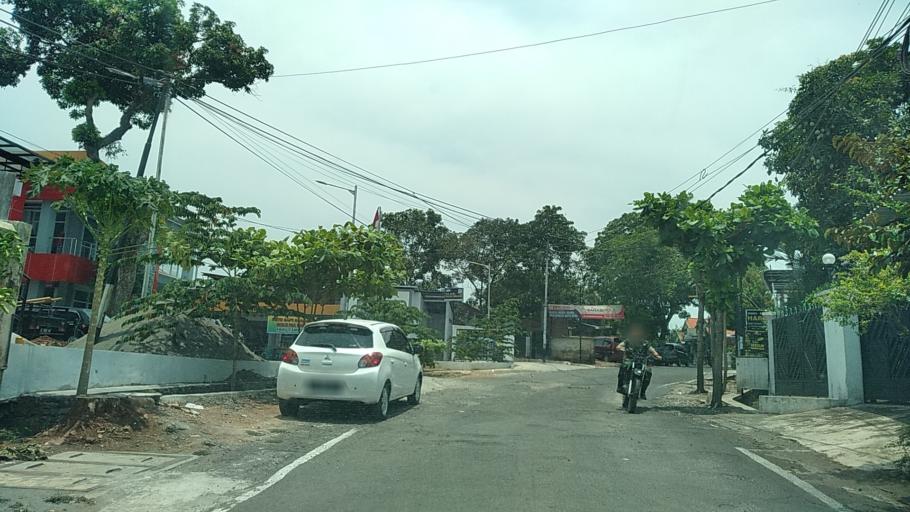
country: ID
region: Central Java
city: Semarang
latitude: -7.0581
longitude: 110.4138
